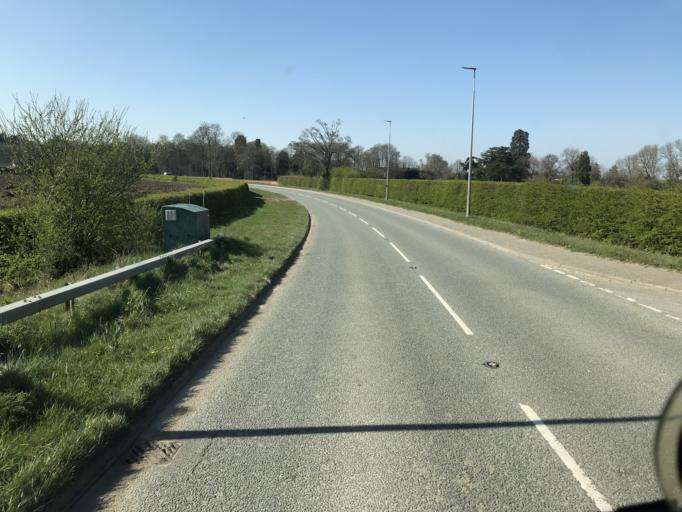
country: GB
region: Wales
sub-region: Wrexham
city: Rossett
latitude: 53.1063
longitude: -2.9604
